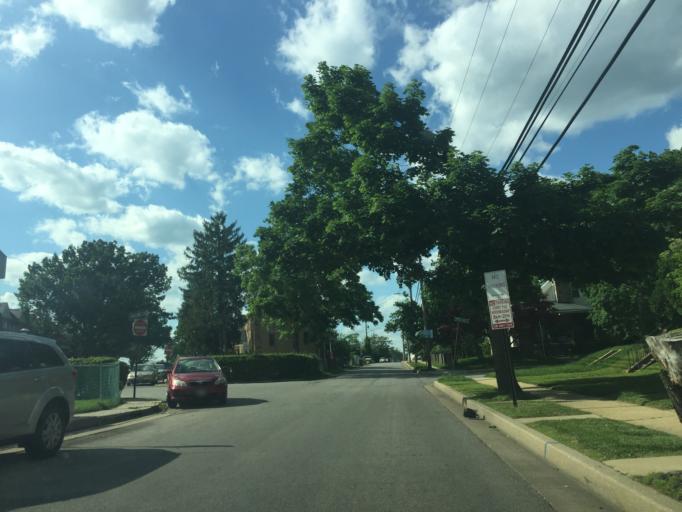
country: US
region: Maryland
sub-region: Baltimore County
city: Lochearn
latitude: 39.3507
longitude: -76.6694
